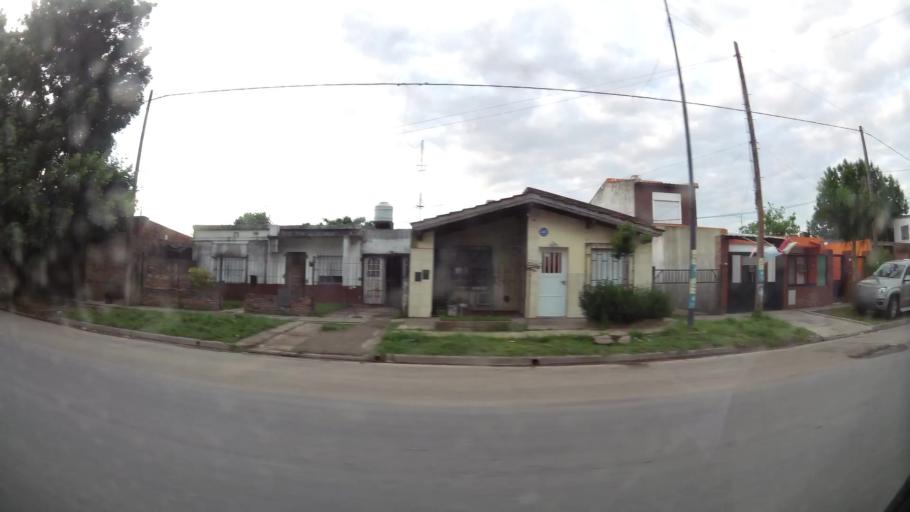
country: AR
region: Buenos Aires
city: San Nicolas de los Arroyos
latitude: -33.3197
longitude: -60.2422
